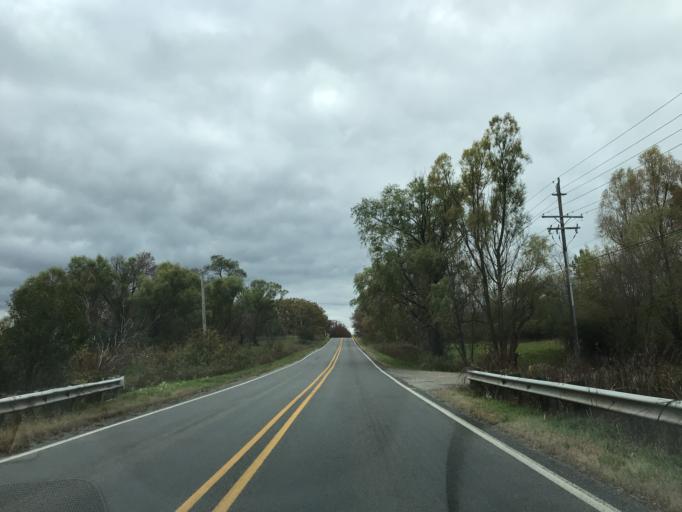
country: US
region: Michigan
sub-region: Washtenaw County
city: Ann Arbor
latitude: 42.3025
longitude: -83.6647
